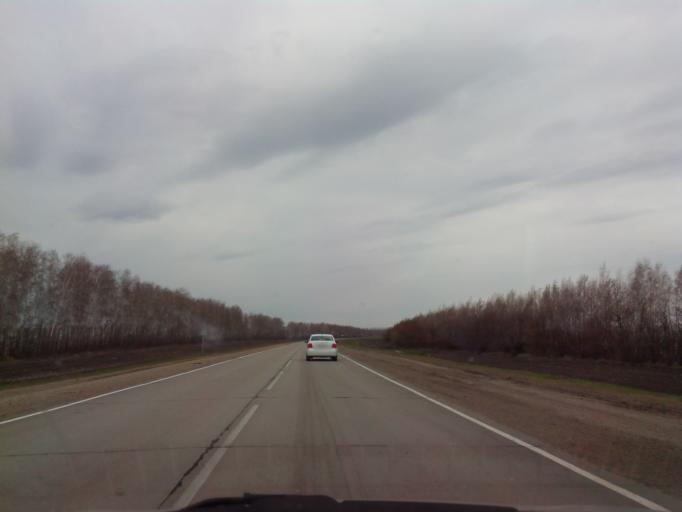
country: RU
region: Tambov
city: Znamenka
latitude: 52.4090
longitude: 41.3835
